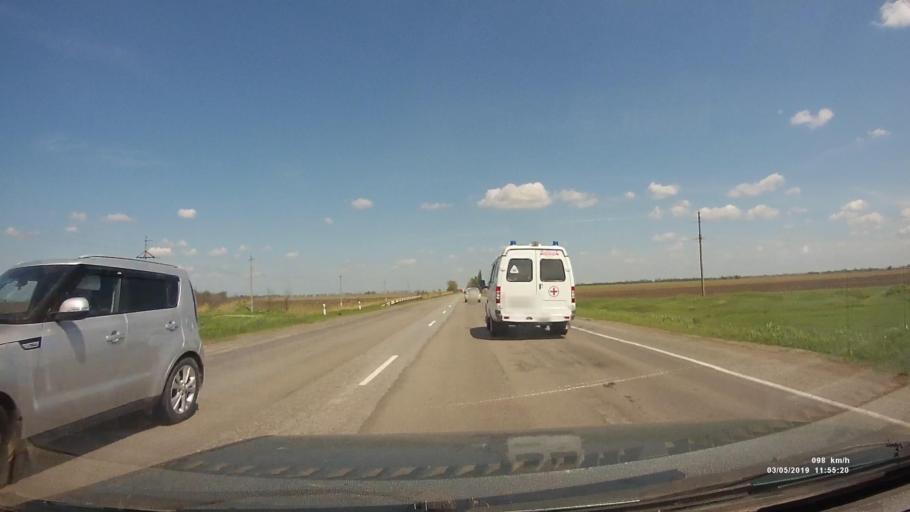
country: RU
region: Rostov
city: Bagayevskaya
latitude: 47.1796
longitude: 40.2901
